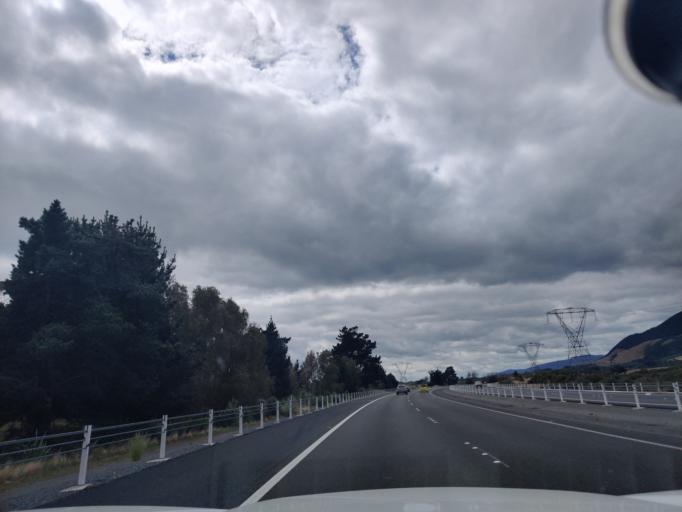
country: NZ
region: Wellington
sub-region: Kapiti Coast District
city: Paraparaumu
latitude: -40.8518
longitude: 175.0611
